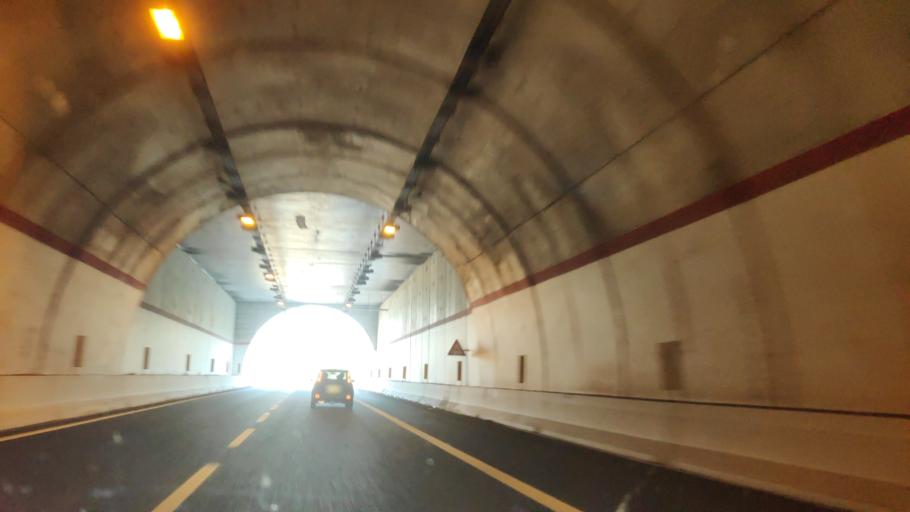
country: IT
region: Basilicate
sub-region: Provincia di Potenza
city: Lauria
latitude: 40.0232
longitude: 15.8790
